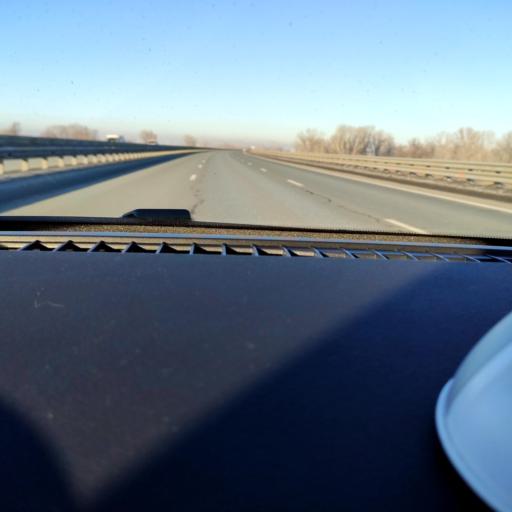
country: RU
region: Samara
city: Smyshlyayevka
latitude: 53.1635
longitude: 50.3231
